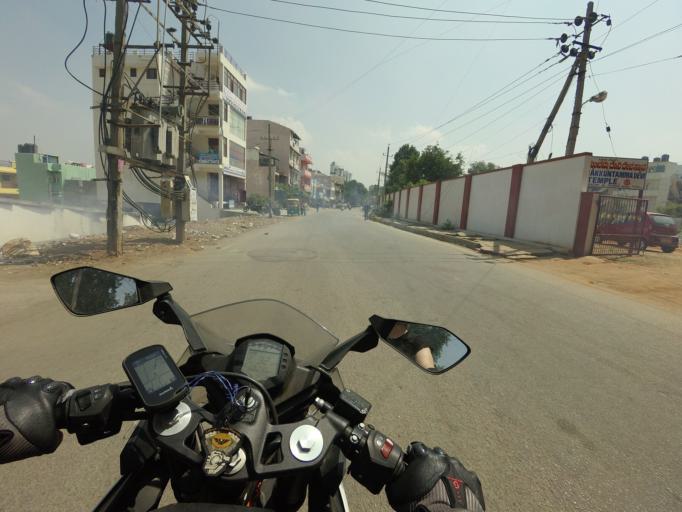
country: IN
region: Karnataka
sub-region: Bangalore Urban
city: Bangalore
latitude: 13.0155
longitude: 77.6543
